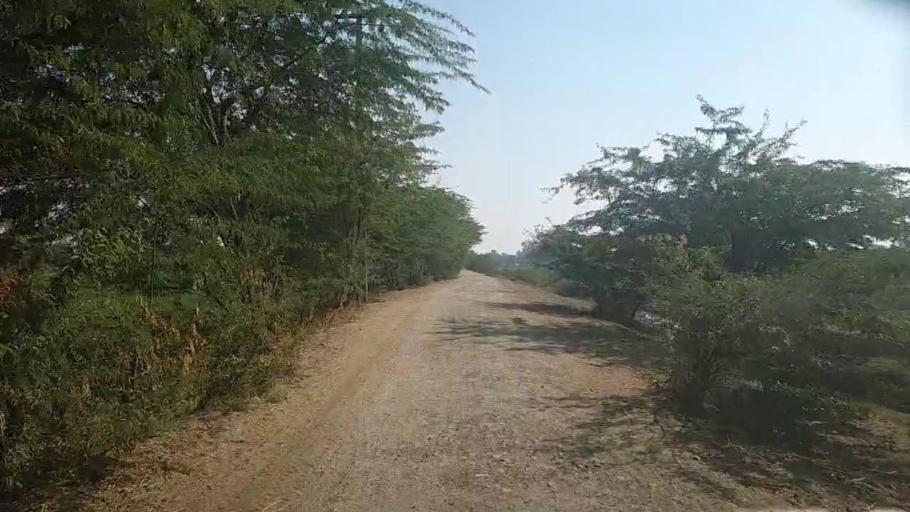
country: PK
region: Sindh
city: Kot Diji
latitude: 27.4370
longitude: 68.7129
